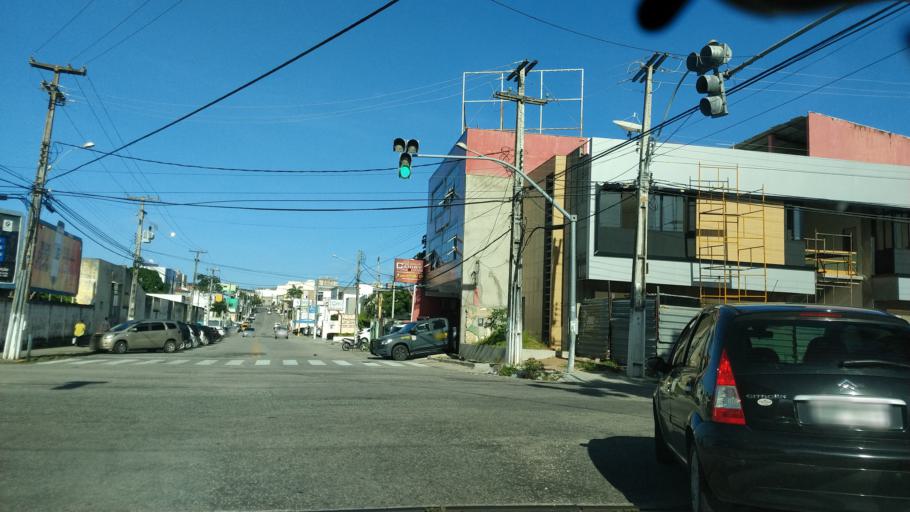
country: BR
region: Rio Grande do Norte
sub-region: Natal
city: Natal
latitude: -5.8247
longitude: -35.2064
